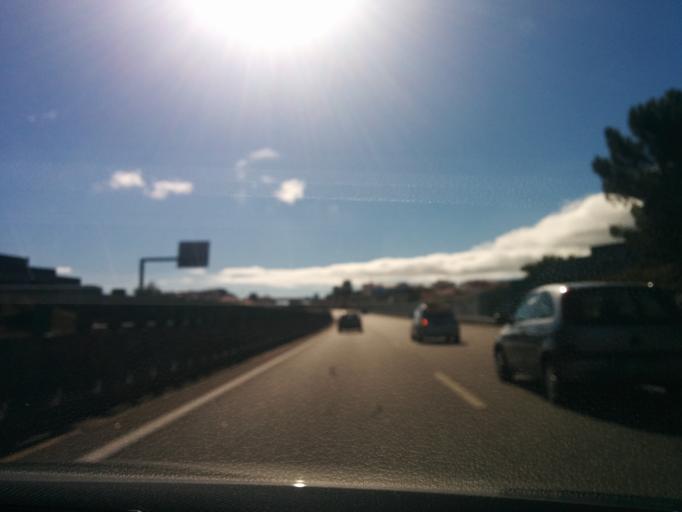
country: PT
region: Lisbon
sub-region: Cascais
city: Estoril
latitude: 38.7181
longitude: -9.3775
